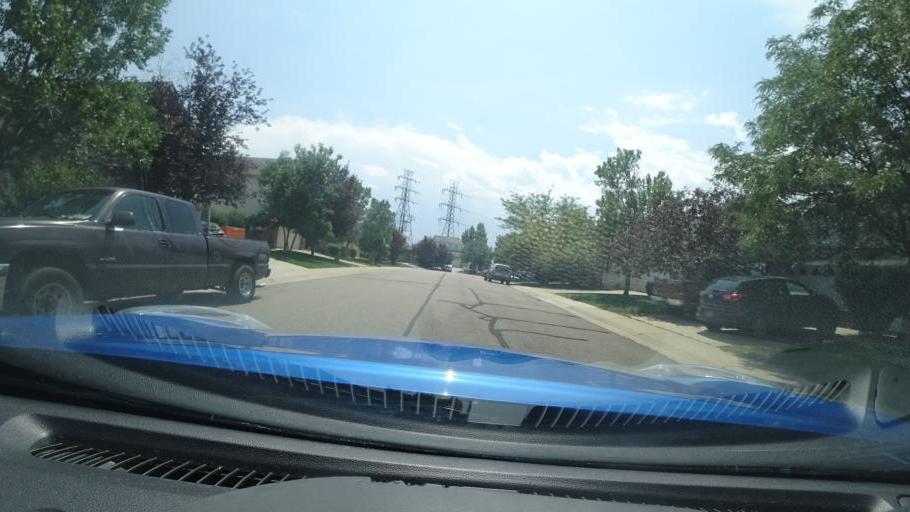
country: US
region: Colorado
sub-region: Adams County
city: Aurora
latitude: 39.6688
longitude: -104.7541
